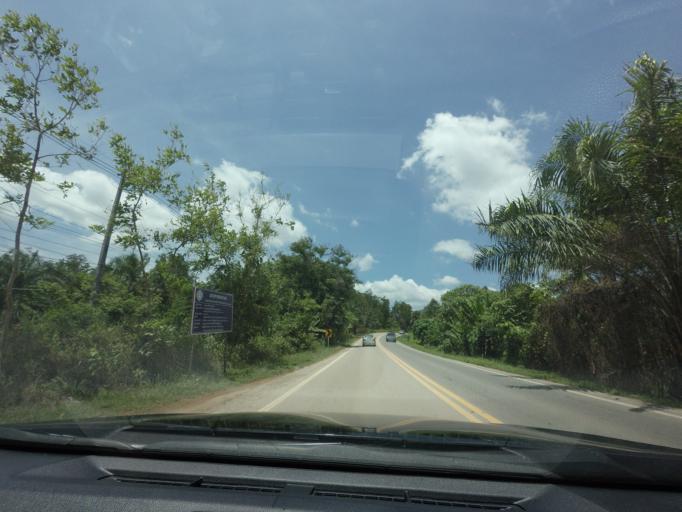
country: TH
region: Chumphon
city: Ban Nam Yuen
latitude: 9.9023
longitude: 98.8949
